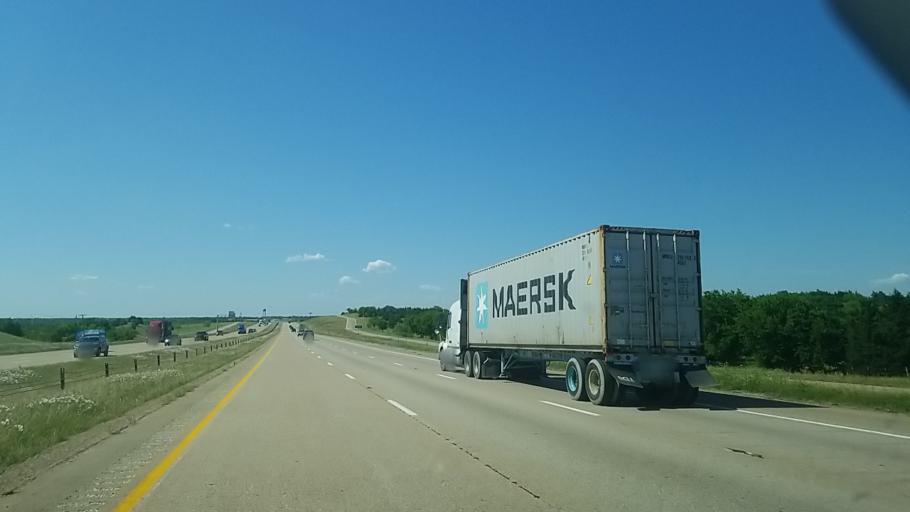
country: US
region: Texas
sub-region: Ellis County
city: Palmer
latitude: 32.3901
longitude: -96.6513
